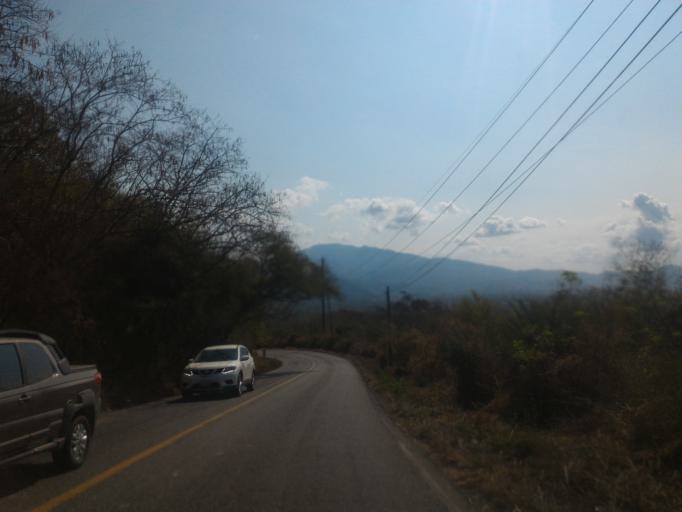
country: MX
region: Michoacan
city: Coahuayana Viejo
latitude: 18.5645
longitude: -103.6374
